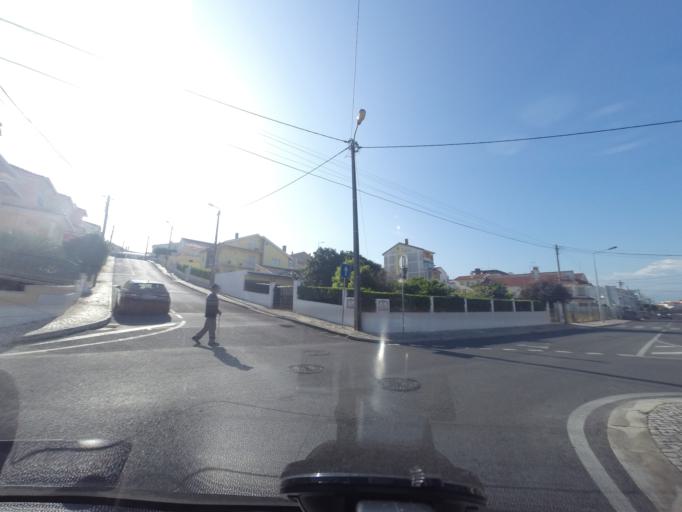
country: PT
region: Lisbon
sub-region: Cascais
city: Sao Domingos de Rana
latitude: 38.7108
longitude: -9.3447
